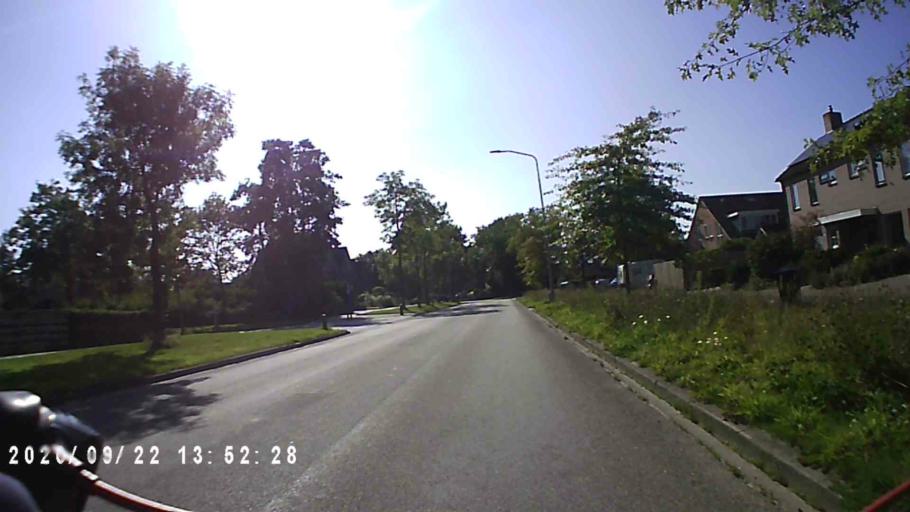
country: NL
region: Groningen
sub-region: Gemeente Leek
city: Leek
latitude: 53.1317
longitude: 6.4140
